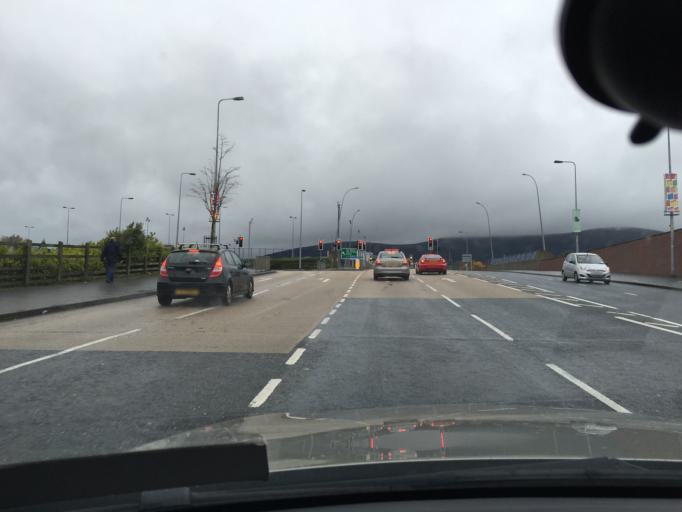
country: GB
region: Northern Ireland
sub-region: City of Belfast
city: Belfast
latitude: 54.5955
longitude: -5.9410
